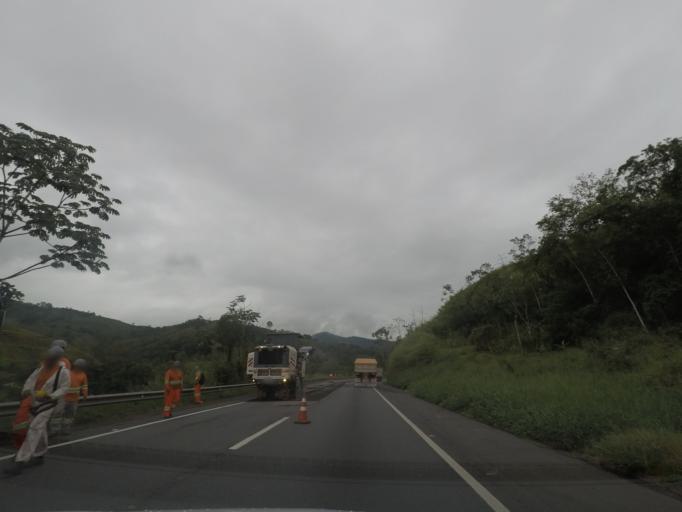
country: BR
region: Sao Paulo
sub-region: Cajati
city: Cajati
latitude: -24.8098
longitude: -48.2121
